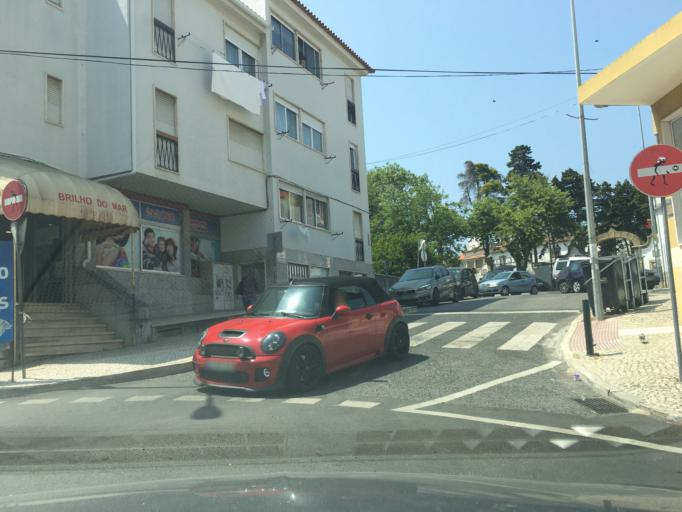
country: PT
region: Lisbon
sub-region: Oeiras
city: Carcavelos
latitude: 38.6907
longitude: -9.3335
